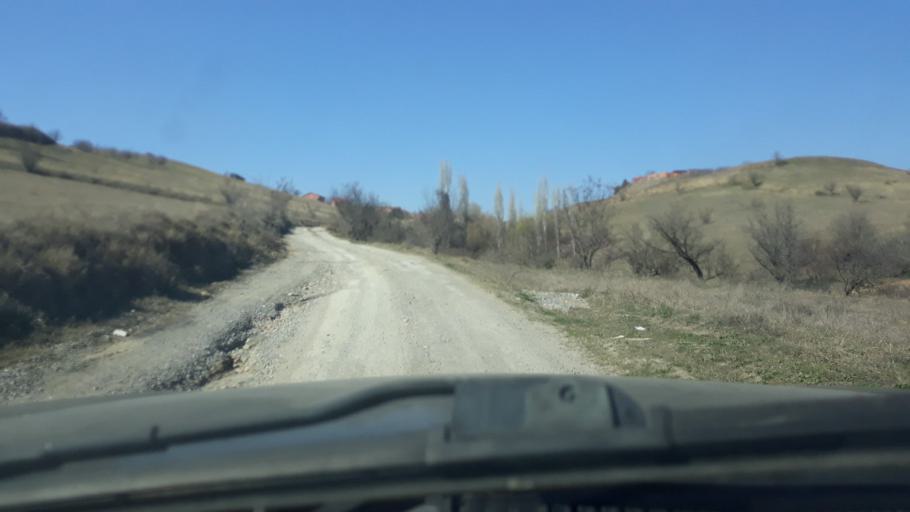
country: MK
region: Veles
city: Gorno Orizari
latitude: 41.6780
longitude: 21.7391
